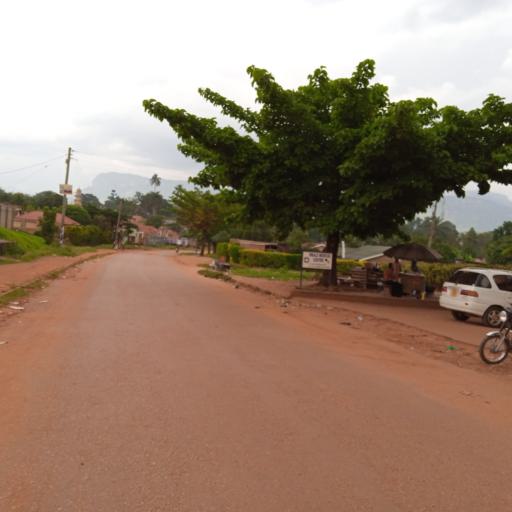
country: UG
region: Eastern Region
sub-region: Mbale District
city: Mbale
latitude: 1.0772
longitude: 34.1698
